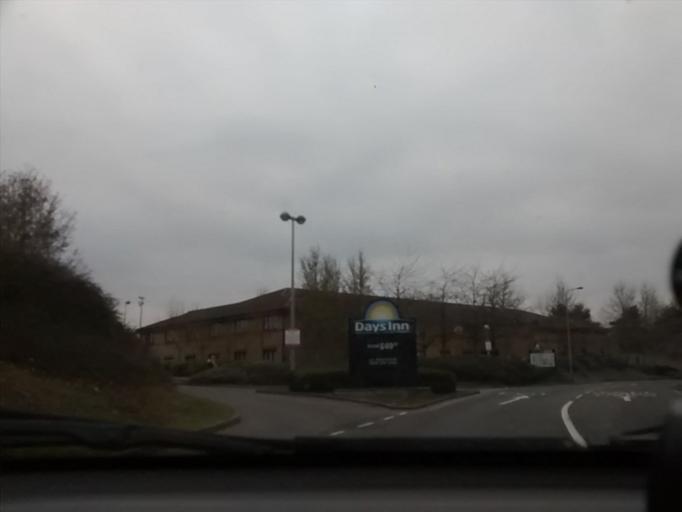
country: GB
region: England
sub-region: Essex
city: Stansted
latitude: 51.8715
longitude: 0.1940
